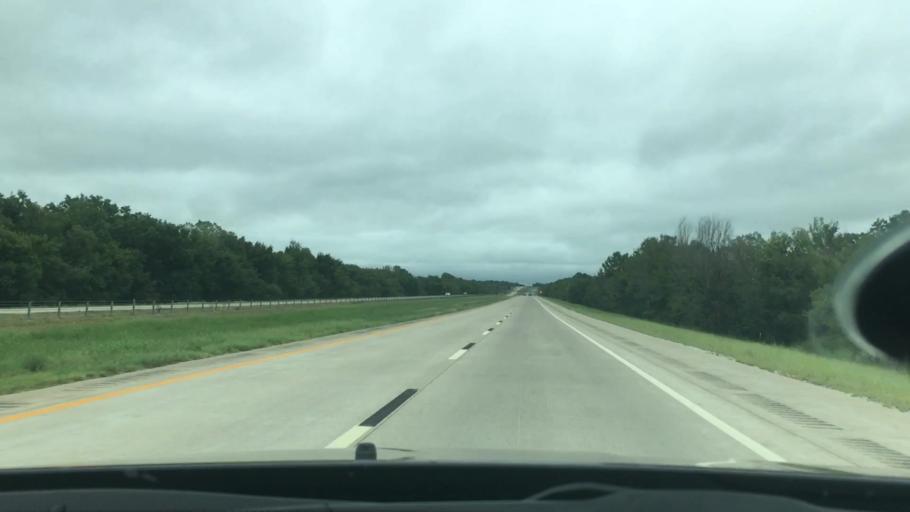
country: US
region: Oklahoma
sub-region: Muskogee County
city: Warner
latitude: 35.4823
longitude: -95.2579
